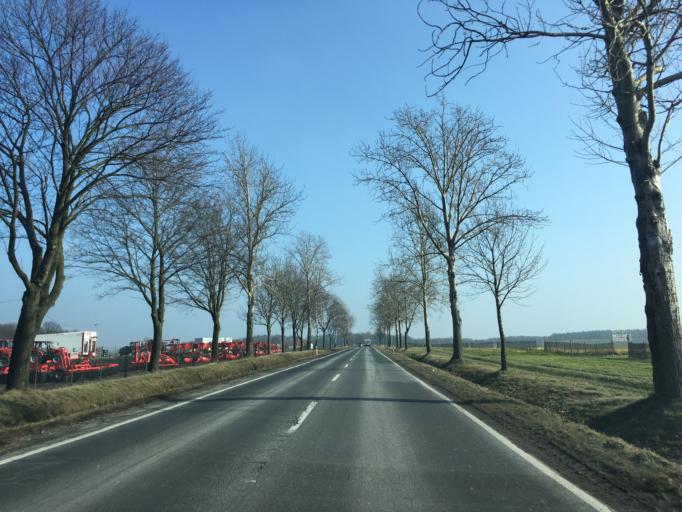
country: PL
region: Lower Silesian Voivodeship
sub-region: Powiat zlotoryjski
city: Olszanica
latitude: 51.2779
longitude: 15.8323
